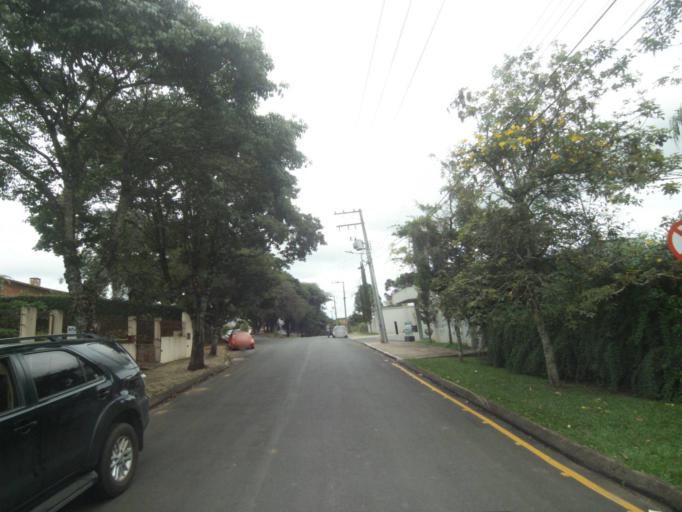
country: BR
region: Parana
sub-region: Telemaco Borba
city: Telemaco Borba
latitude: -24.3301
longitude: -50.6105
